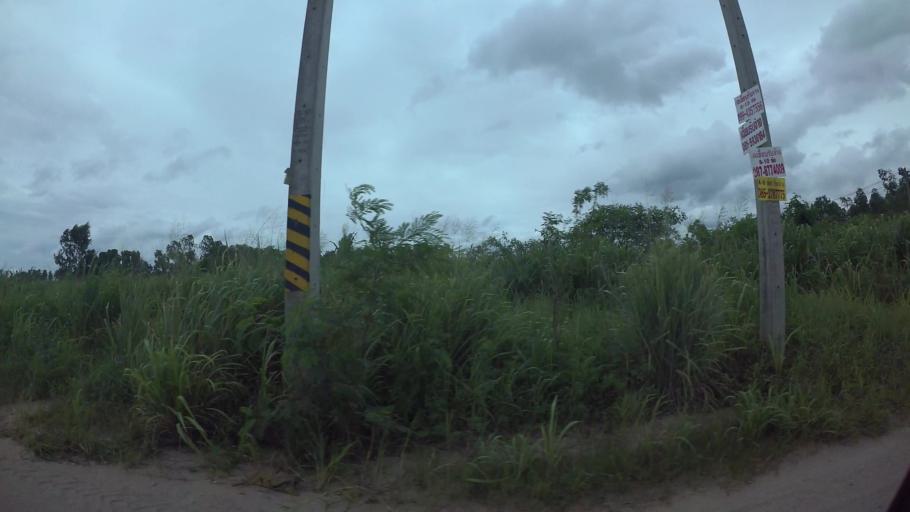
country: TH
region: Chon Buri
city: Si Racha
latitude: 13.1759
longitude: 100.9825
